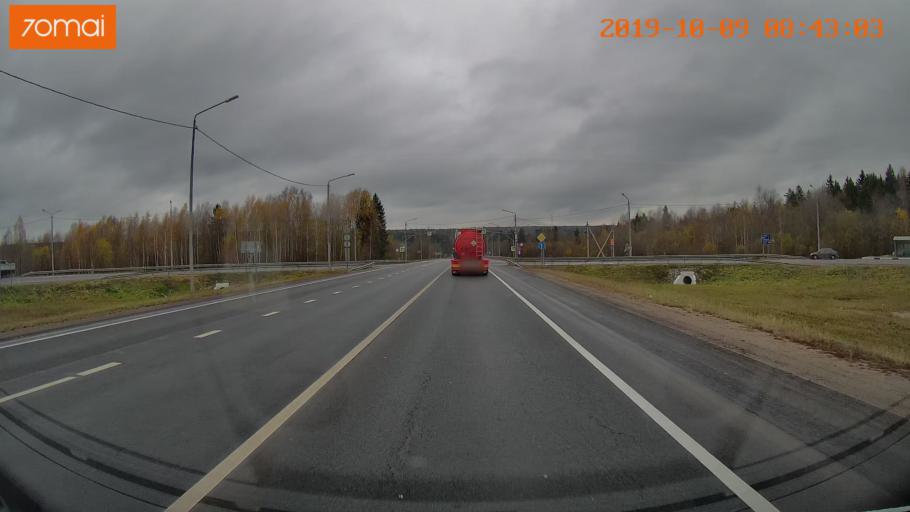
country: RU
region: Vologda
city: Gryazovets
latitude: 59.0207
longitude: 40.1161
